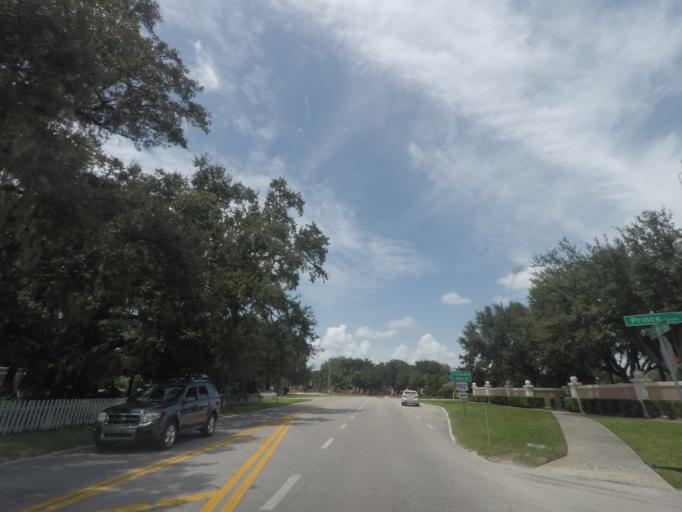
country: US
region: Florida
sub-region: Osceola County
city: Kissimmee
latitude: 28.3149
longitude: -81.4618
